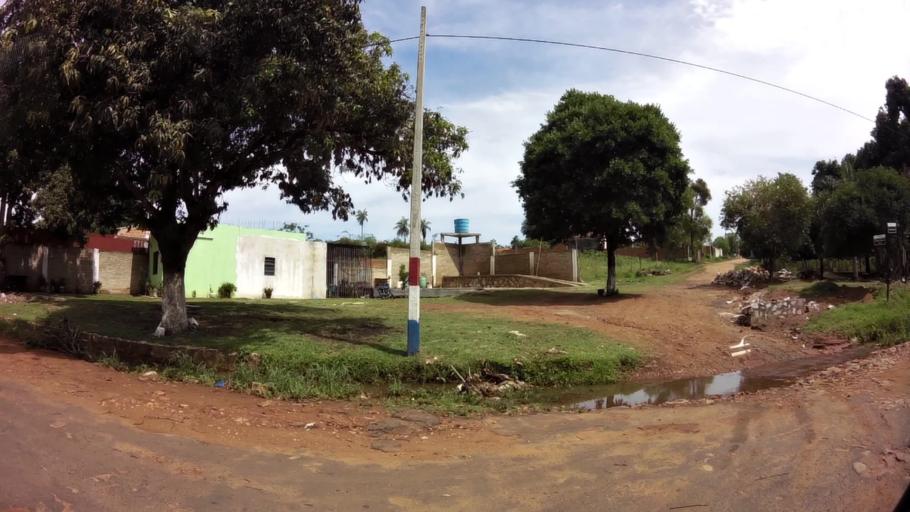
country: PY
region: Central
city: Limpio
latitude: -25.1795
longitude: -57.4429
